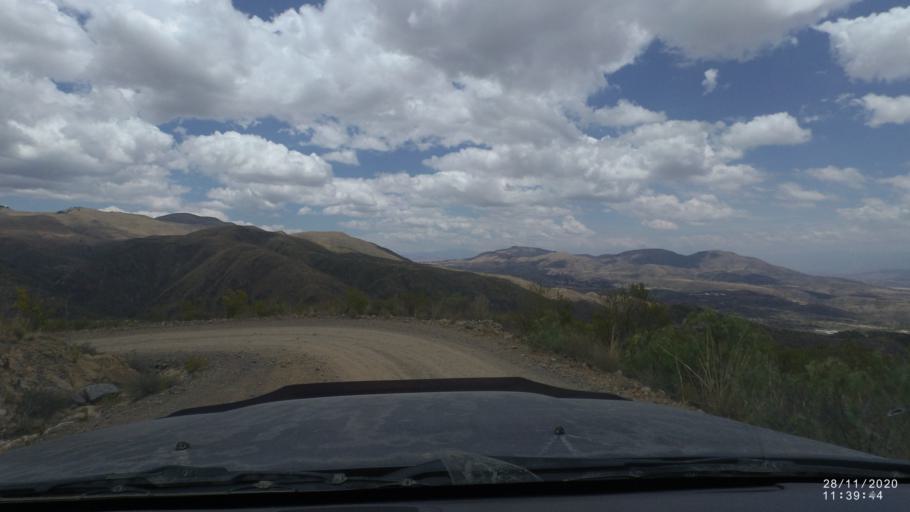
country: BO
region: Cochabamba
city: Tarata
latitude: -17.6742
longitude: -66.0441
